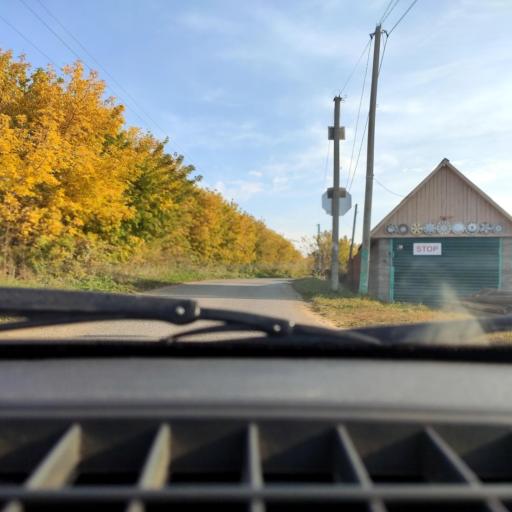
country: RU
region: Bashkortostan
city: Avdon
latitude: 54.6390
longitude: 55.7304
